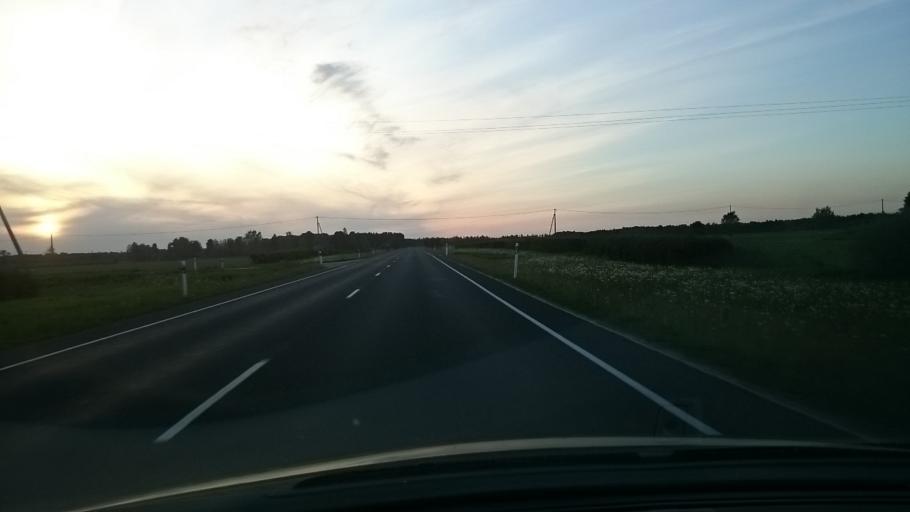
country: EE
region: Viljandimaa
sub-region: Vohma linn
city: Vohma
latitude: 58.7005
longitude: 25.6244
